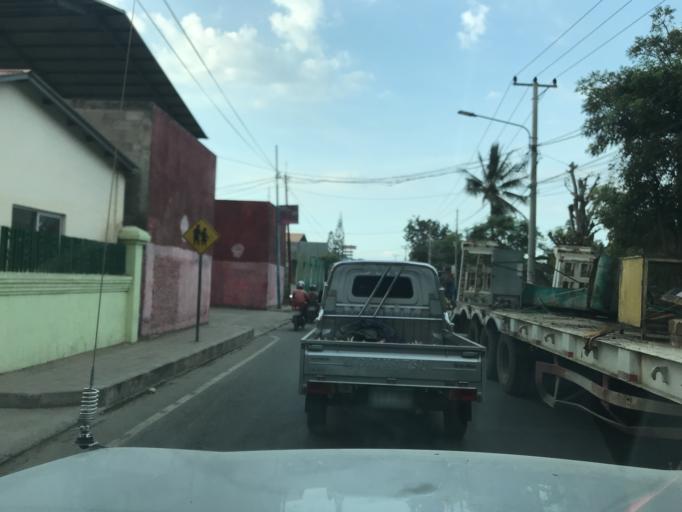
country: TL
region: Dili
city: Dili
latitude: -8.5508
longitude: 125.5433
